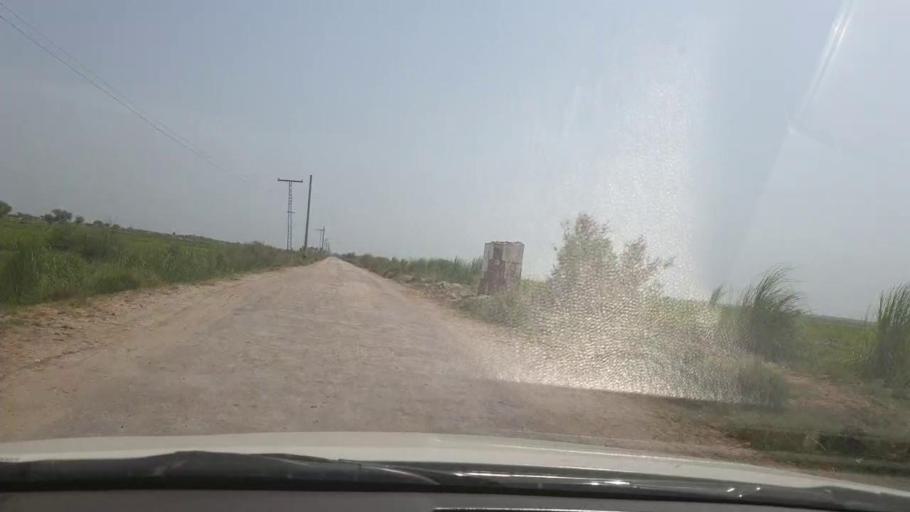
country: PK
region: Sindh
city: Garhi Yasin
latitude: 27.9678
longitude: 68.5040
